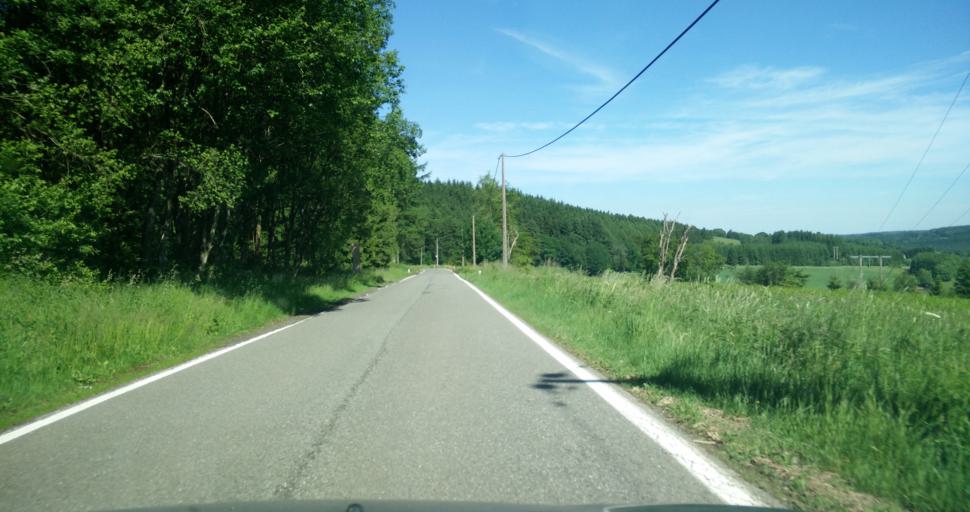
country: BE
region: Wallonia
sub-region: Province du Luxembourg
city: La Roche-en-Ardenne
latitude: 50.2204
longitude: 5.6273
